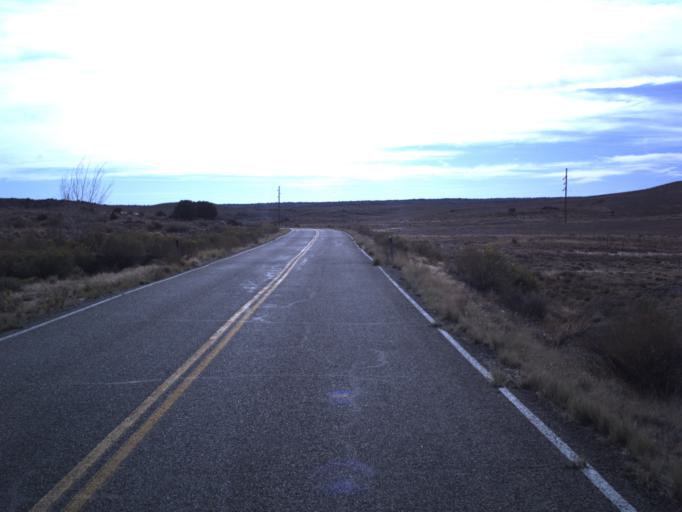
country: US
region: Utah
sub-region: San Juan County
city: Blanding
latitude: 37.4190
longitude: -109.4353
